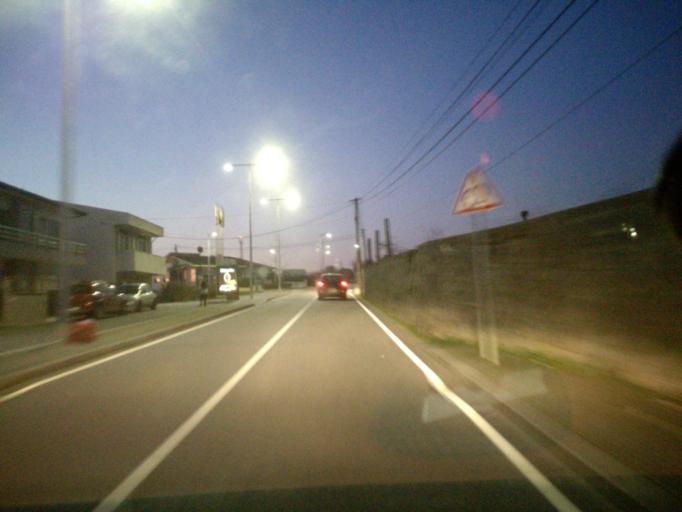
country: PT
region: Porto
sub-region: Maia
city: Nogueira
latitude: 41.2523
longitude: -8.5829
